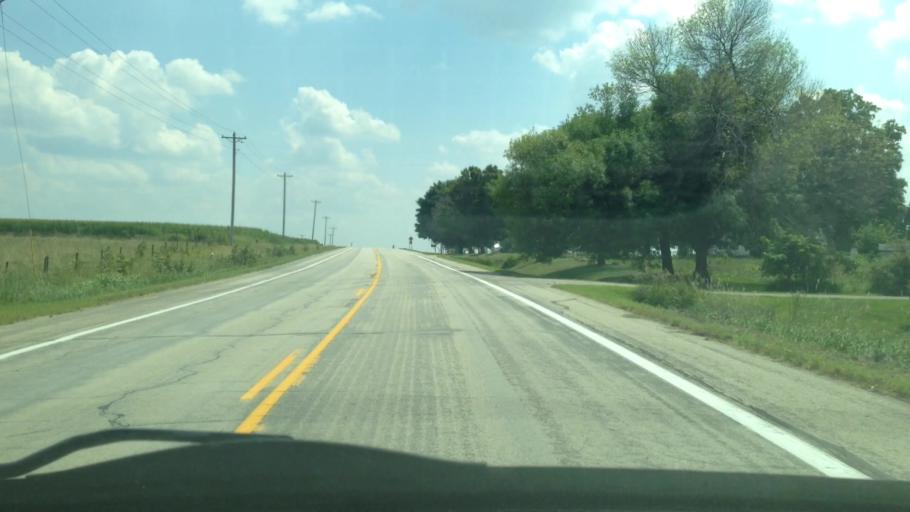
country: US
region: Minnesota
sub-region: Olmsted County
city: Rochester
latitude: 43.9609
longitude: -92.4295
